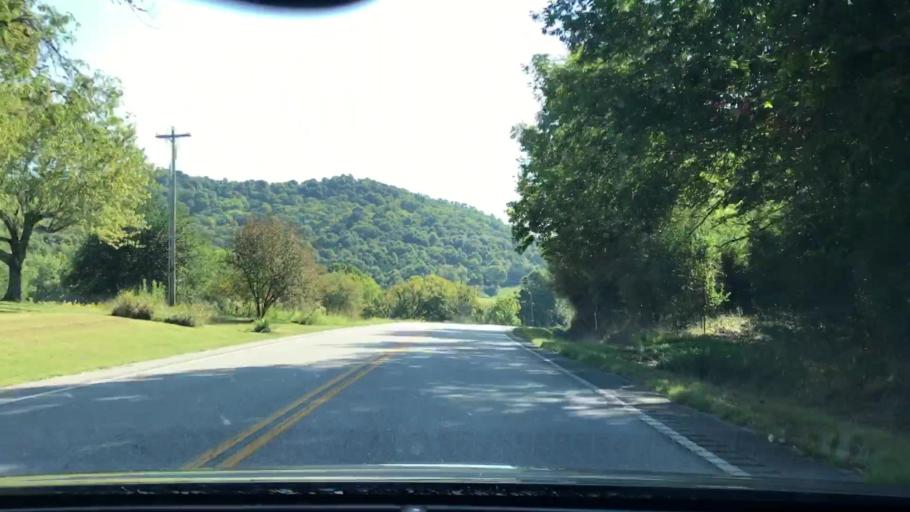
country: US
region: Tennessee
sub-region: Jackson County
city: Gainesboro
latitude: 36.3586
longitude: -85.7392
